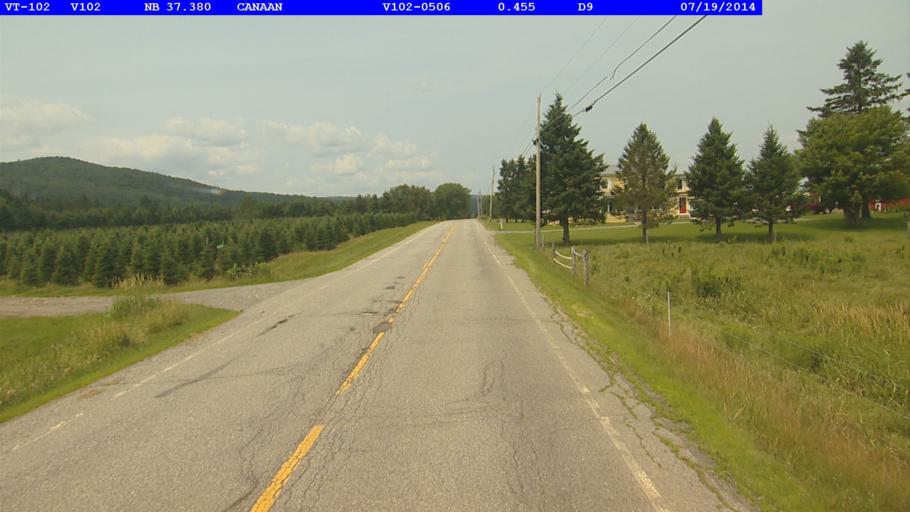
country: US
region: New Hampshire
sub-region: Coos County
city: Colebrook
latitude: 44.9160
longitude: -71.5126
